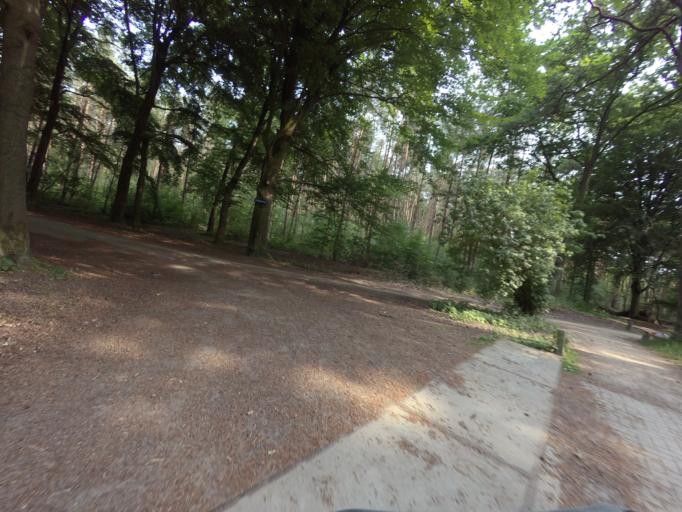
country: NL
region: North Holland
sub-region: Gemeente Hilversum
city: Hilversum
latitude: 52.1767
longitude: 5.2122
